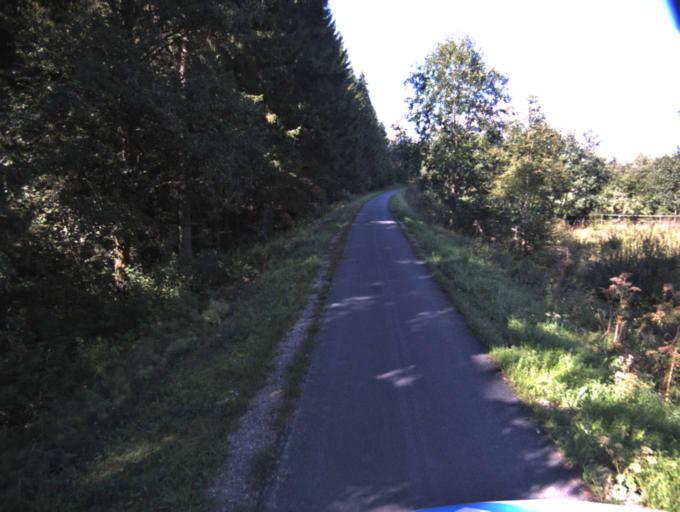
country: SE
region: Vaestra Goetaland
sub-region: Ulricehamns Kommun
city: Ulricehamn
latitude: 57.8064
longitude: 13.3579
